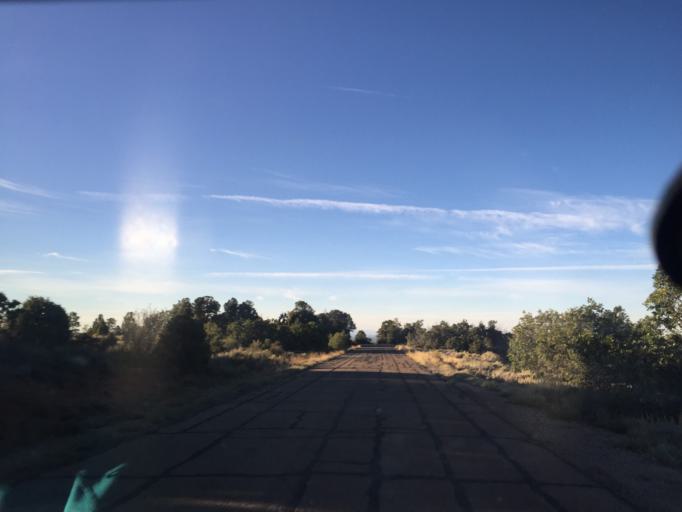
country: US
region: Utah
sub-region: San Juan County
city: Blanding
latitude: 37.7310
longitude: -109.4142
